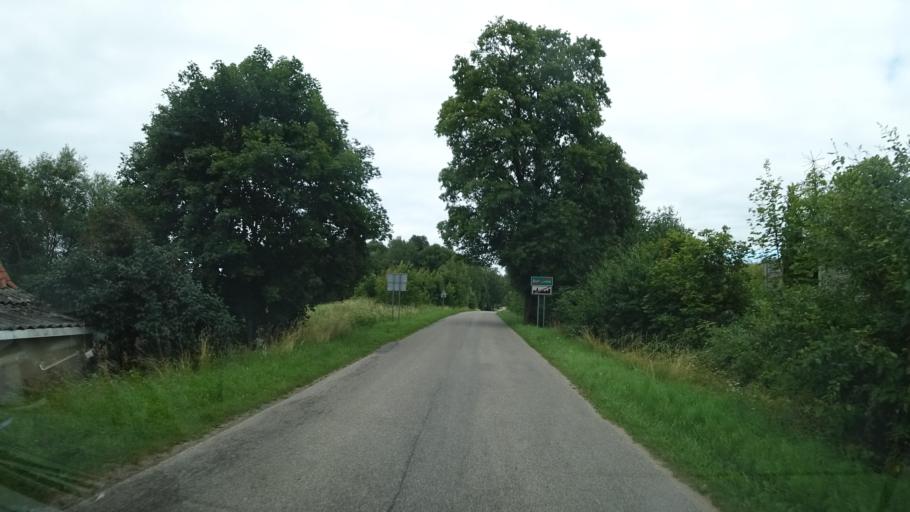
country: PL
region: Podlasie
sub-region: Powiat suwalski
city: Filipow
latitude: 54.2877
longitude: 22.5687
